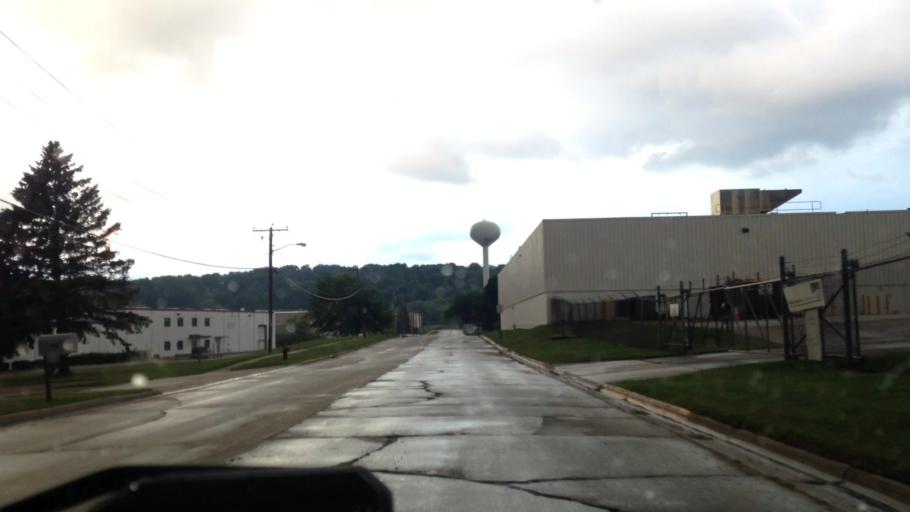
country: US
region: Wisconsin
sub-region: Dodge County
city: Mayville
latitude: 43.4868
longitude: -88.5505
